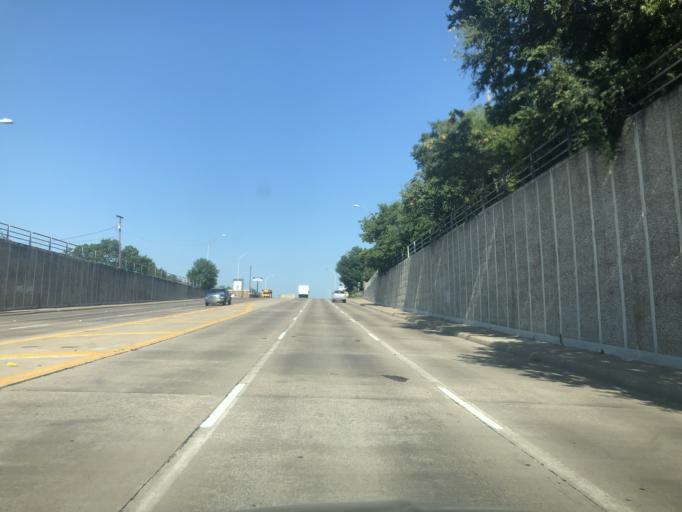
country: US
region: Texas
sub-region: Tarrant County
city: Fort Worth
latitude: 32.7061
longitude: -97.3391
